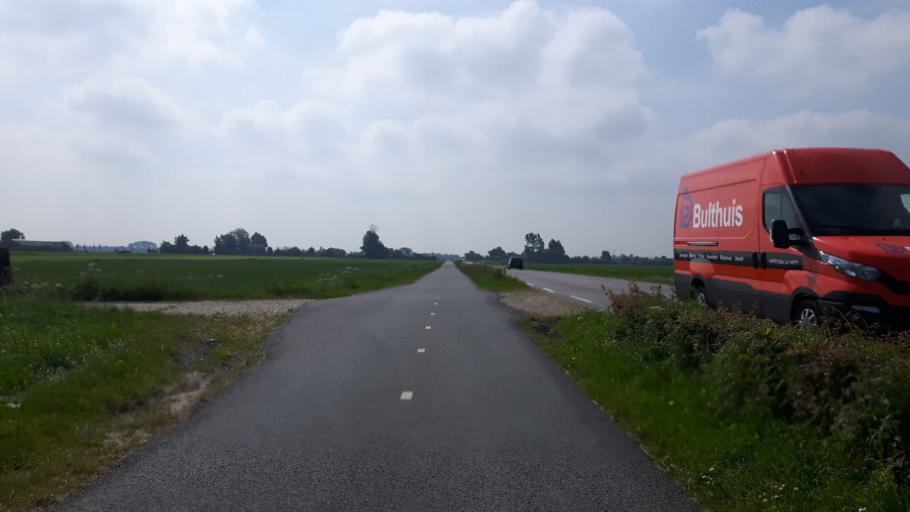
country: NL
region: Utrecht
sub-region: Gemeente Montfoort
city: Montfoort
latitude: 52.0310
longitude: 4.9418
